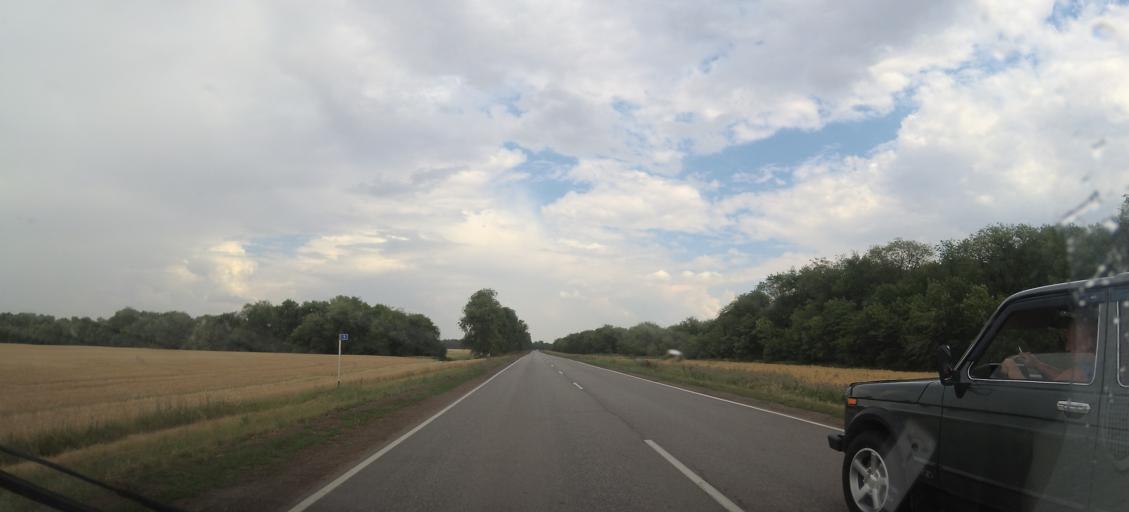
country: RU
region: Rostov
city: Peschanokopskoye
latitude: 46.2015
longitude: 41.1894
